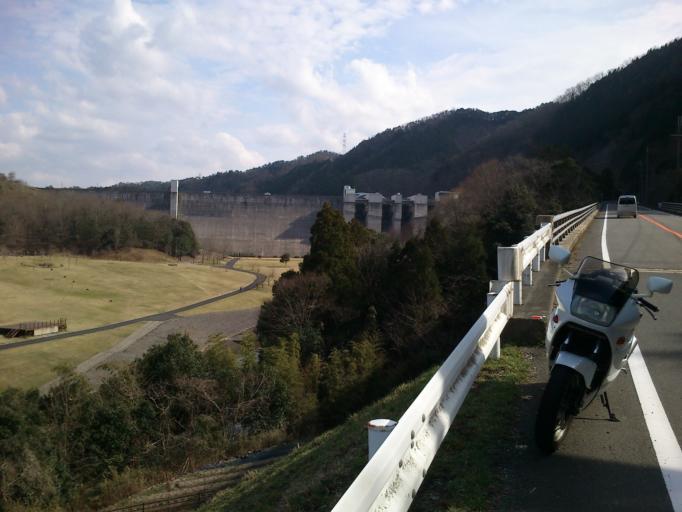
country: JP
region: Kyoto
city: Kameoka
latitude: 35.1519
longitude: 135.5157
